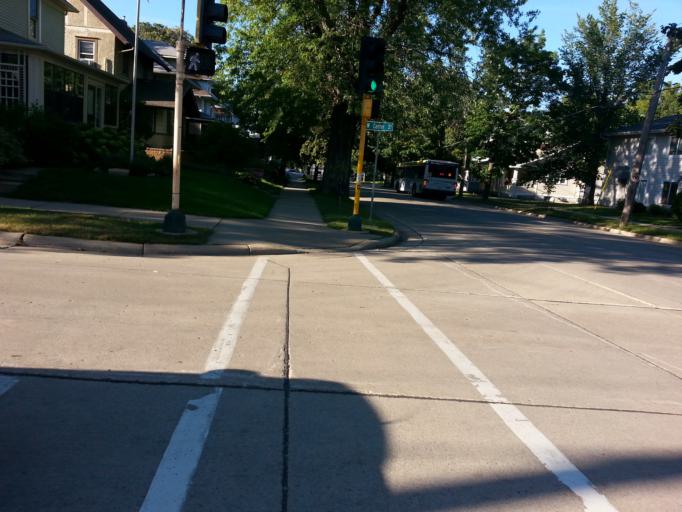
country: US
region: Minnesota
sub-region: Olmsted County
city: Rochester
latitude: 44.0235
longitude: -92.4790
